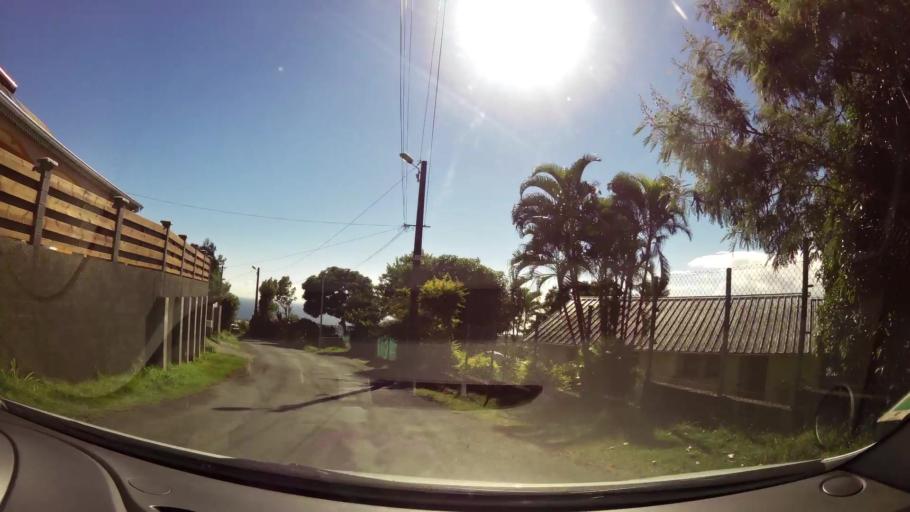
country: RE
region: Reunion
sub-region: Reunion
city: Saint-Denis
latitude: -20.9185
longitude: 55.4862
